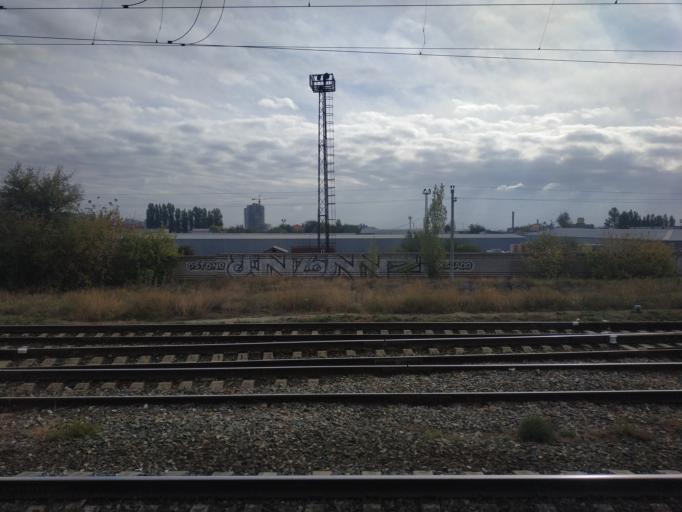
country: RU
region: Volgograd
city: Volgograd
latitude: 48.6731
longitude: 44.4642
